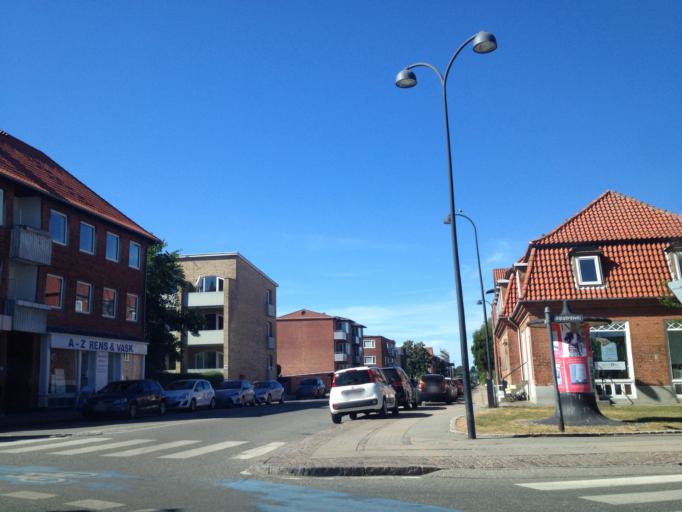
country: DK
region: Capital Region
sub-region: Gentofte Kommune
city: Charlottenlund
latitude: 55.7599
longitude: 12.5856
